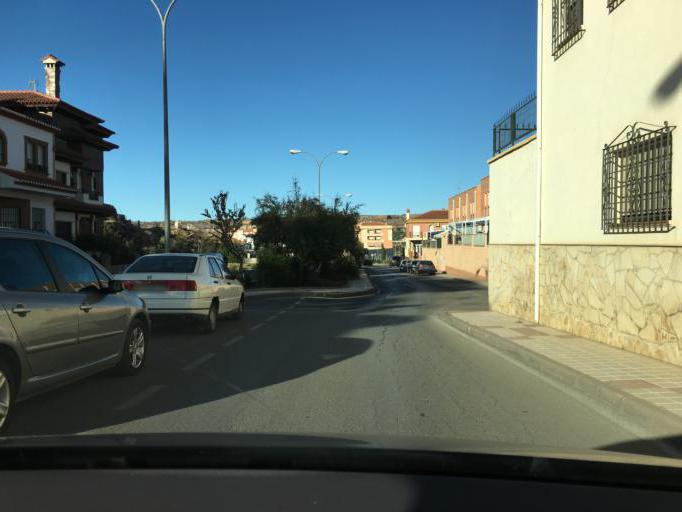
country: ES
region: Andalusia
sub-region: Provincia de Granada
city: Guadix
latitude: 37.2957
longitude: -3.1307
